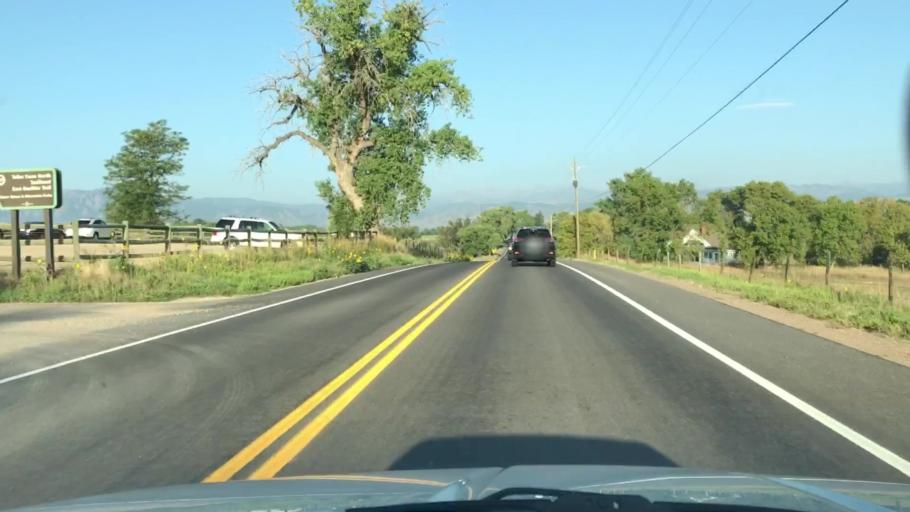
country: US
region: Colorado
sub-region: Boulder County
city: Gunbarrel
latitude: 40.0401
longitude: -105.1422
